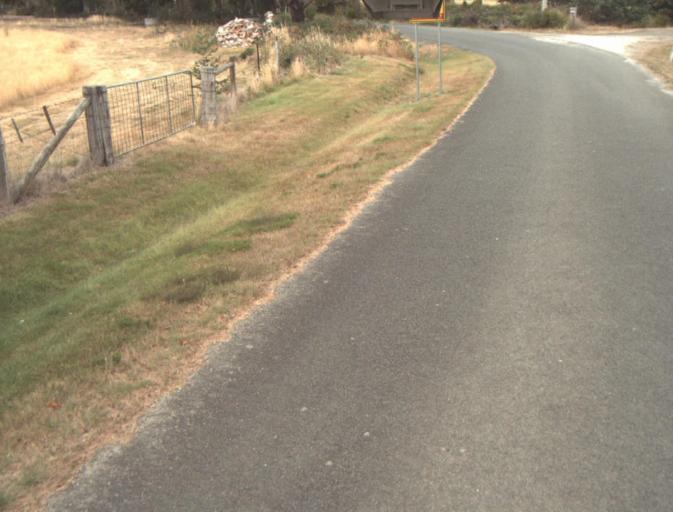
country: AU
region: Tasmania
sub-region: Launceston
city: Mayfield
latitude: -41.2699
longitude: 147.1675
